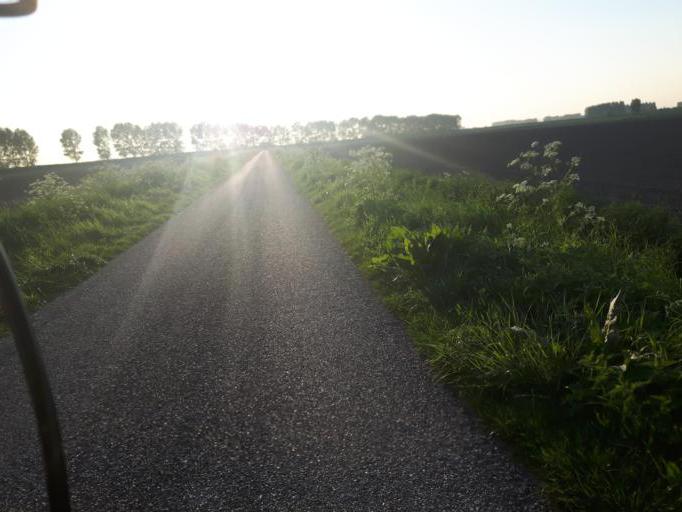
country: NL
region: Zeeland
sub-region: Gemeente Goes
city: Goes
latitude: 51.5095
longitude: 3.8129
